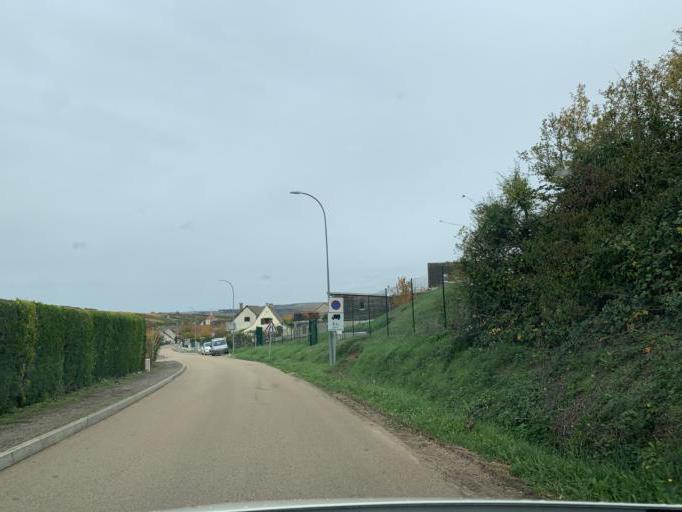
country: FR
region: Bourgogne
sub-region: Departement de l'Yonne
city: Champs-sur-Yonne
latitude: 47.7184
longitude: 3.5798
